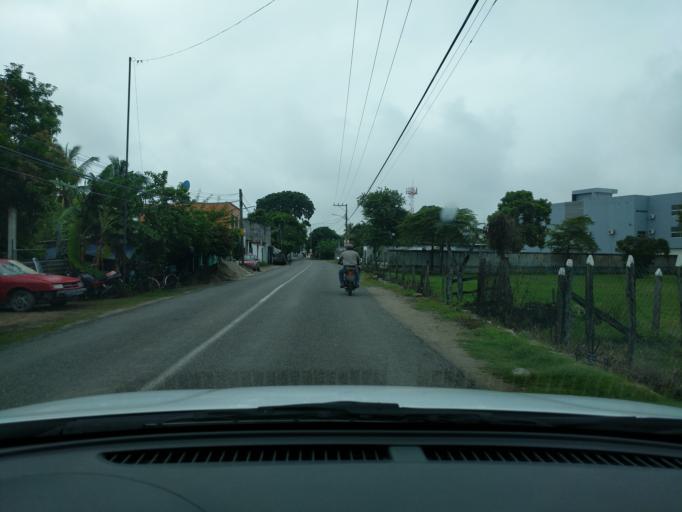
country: MX
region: Tabasco
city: Villahermosa
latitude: 17.9569
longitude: -92.9648
